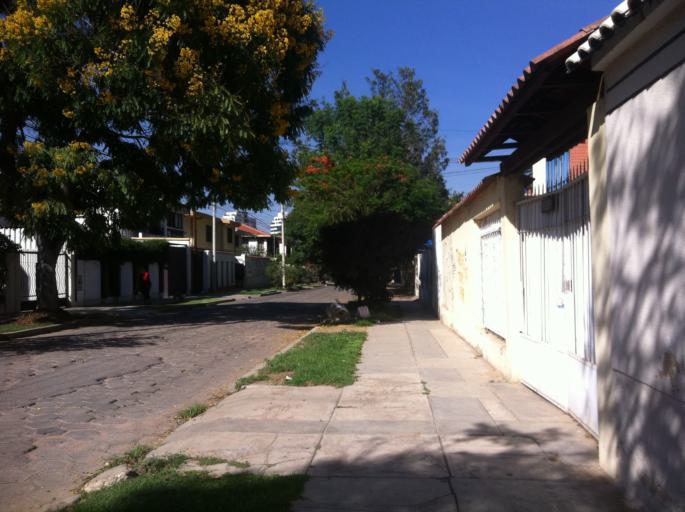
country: BO
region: Cochabamba
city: Cochabamba
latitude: -17.3811
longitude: -66.1485
